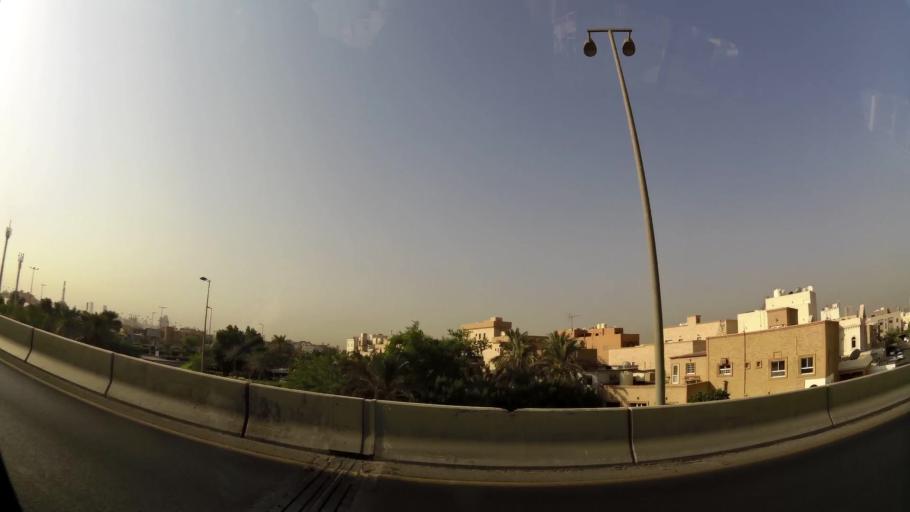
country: KW
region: Al Asimah
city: Ad Dasmah
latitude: 29.3661
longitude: 48.0102
